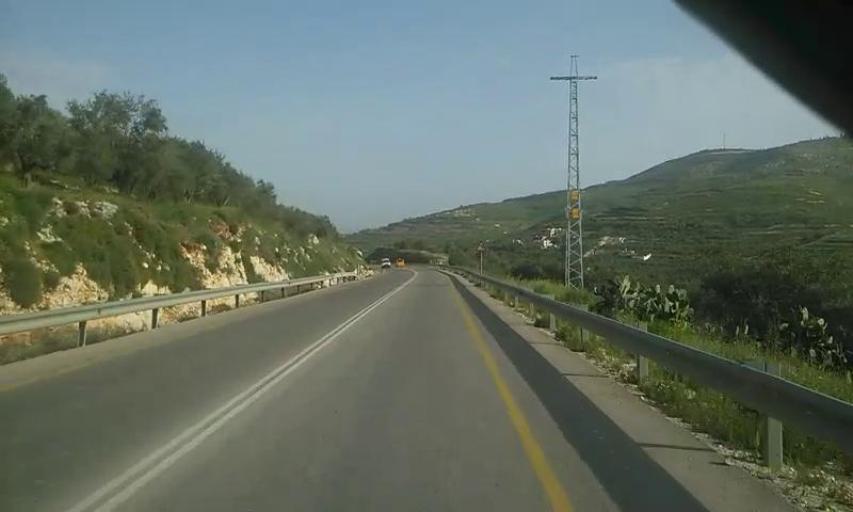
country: PS
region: West Bank
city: Madama
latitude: 32.1862
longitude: 35.2335
